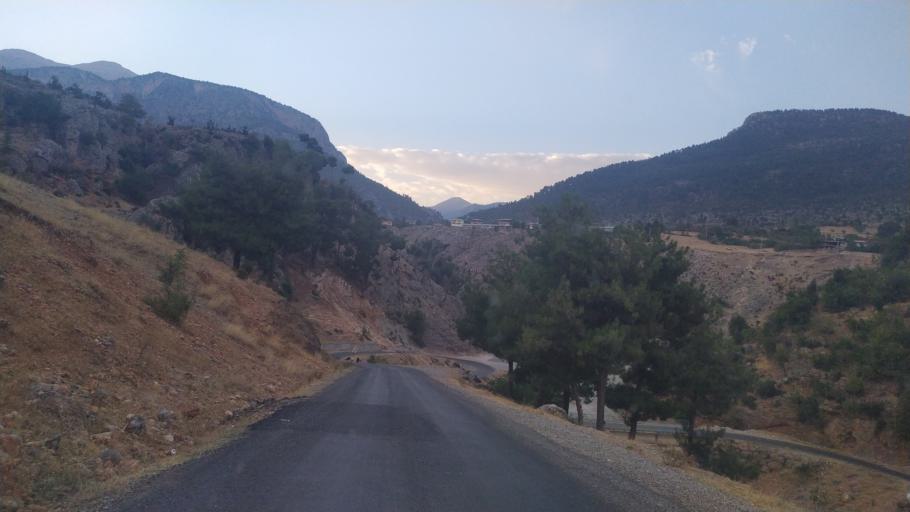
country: TR
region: Mersin
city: Camliyayla
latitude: 37.2386
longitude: 34.7138
